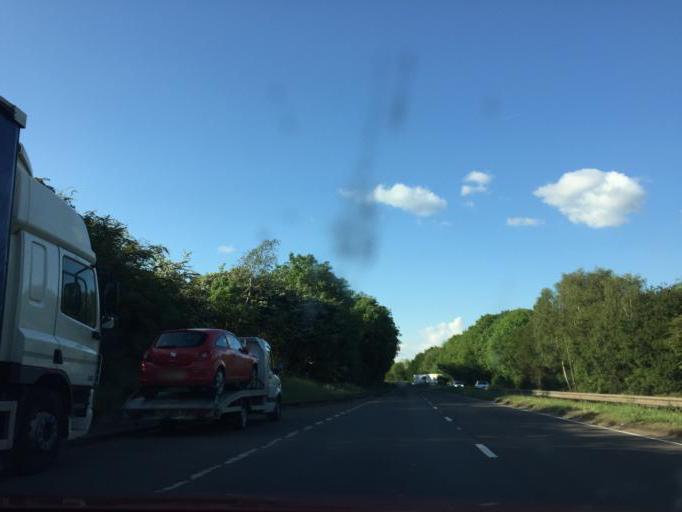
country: GB
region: England
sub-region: Warwickshire
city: Exhall
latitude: 52.4676
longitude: -1.4904
